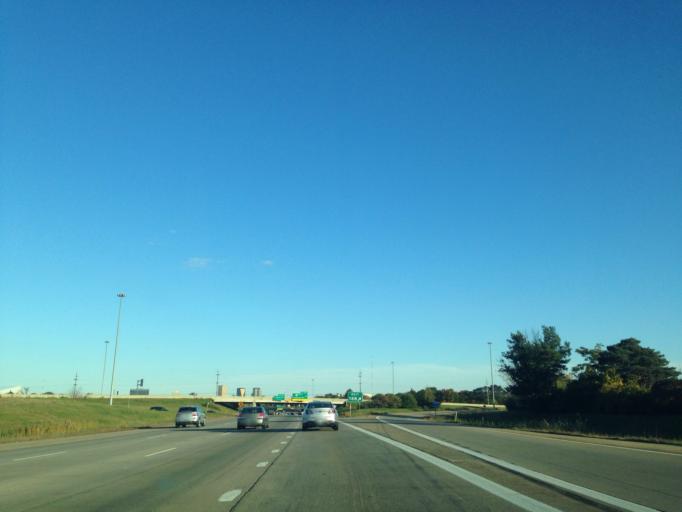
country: US
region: Michigan
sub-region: Oakland County
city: Bingham Farms
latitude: 42.4895
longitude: -83.2881
